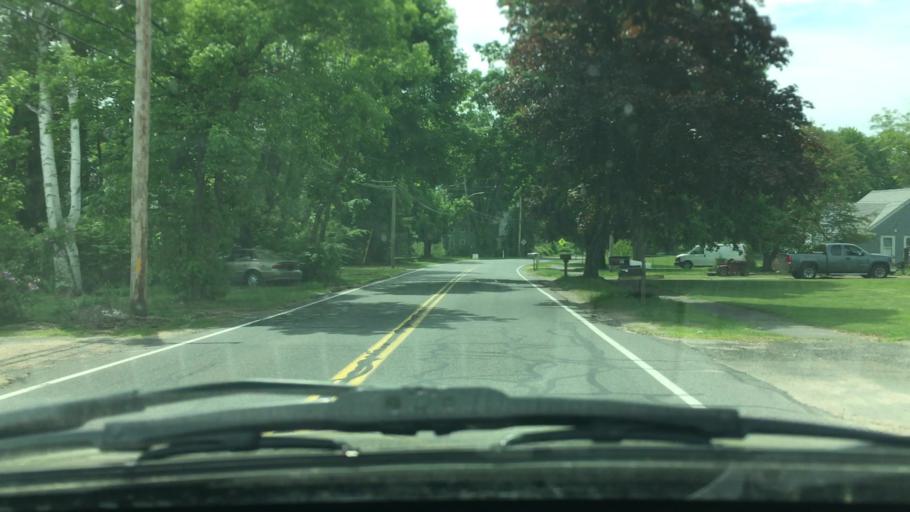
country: US
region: Massachusetts
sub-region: Hampshire County
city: Belchertown
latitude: 42.2704
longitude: -72.3977
